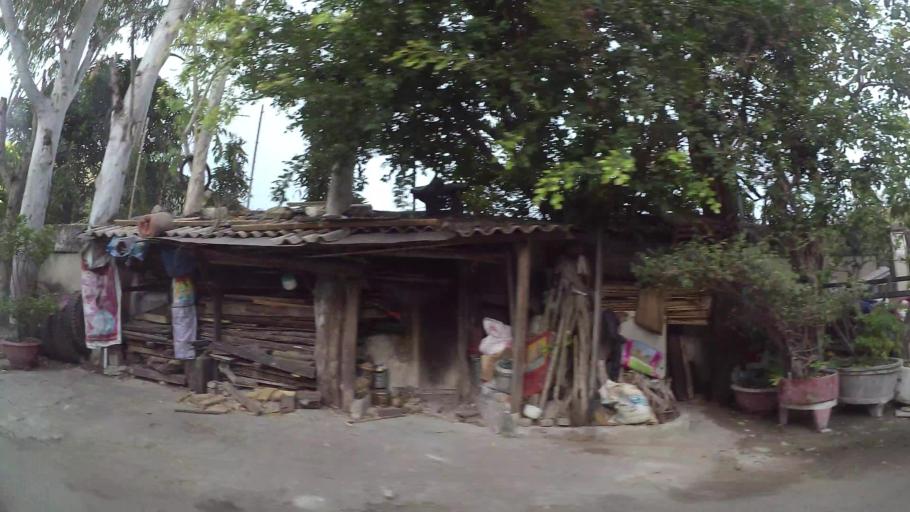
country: VN
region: Da Nang
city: Son Tra
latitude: 16.0809
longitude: 108.2396
